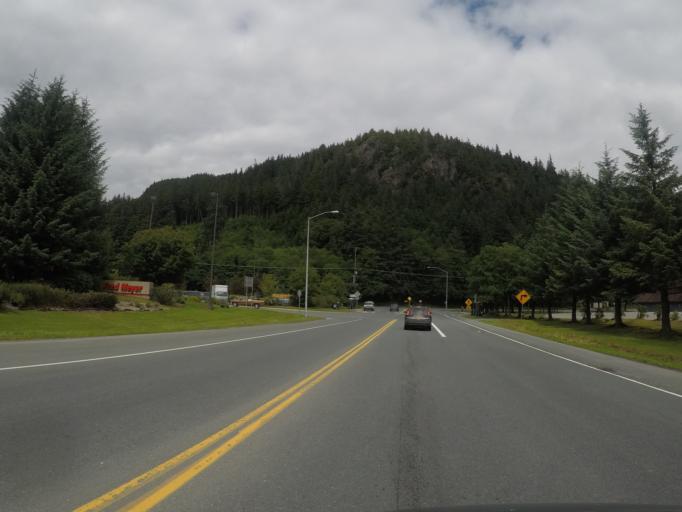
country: US
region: Alaska
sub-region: Juneau City and Borough
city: Juneau
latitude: 58.3588
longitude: -134.5585
